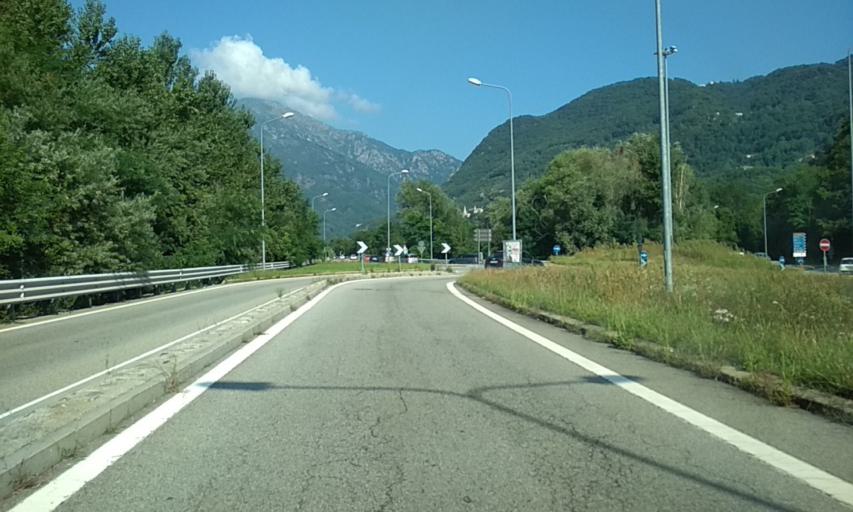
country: IT
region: Piedmont
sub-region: Provincia di Torino
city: Pont-Canavese
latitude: 45.4127
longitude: 7.6193
